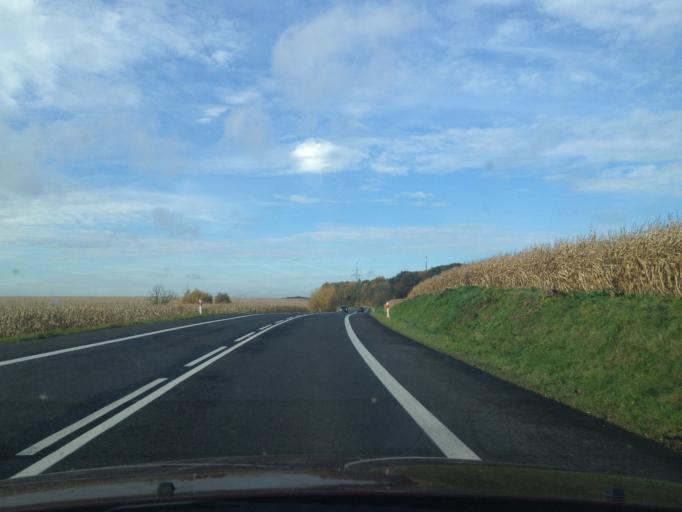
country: PL
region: Lower Silesian Voivodeship
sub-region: Powiat lubanski
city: Siekierczyn
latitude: 51.1455
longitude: 15.1978
